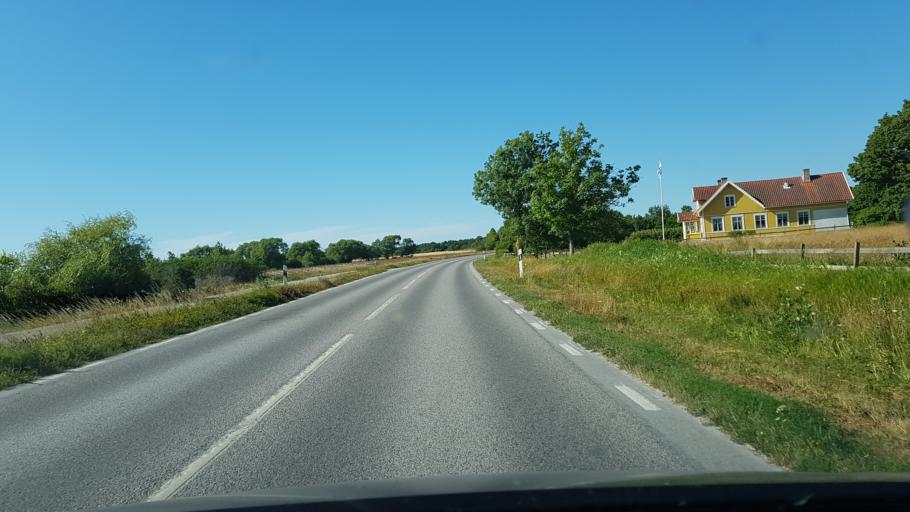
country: SE
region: Gotland
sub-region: Gotland
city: Klintehamn
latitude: 57.4566
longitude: 18.1297
